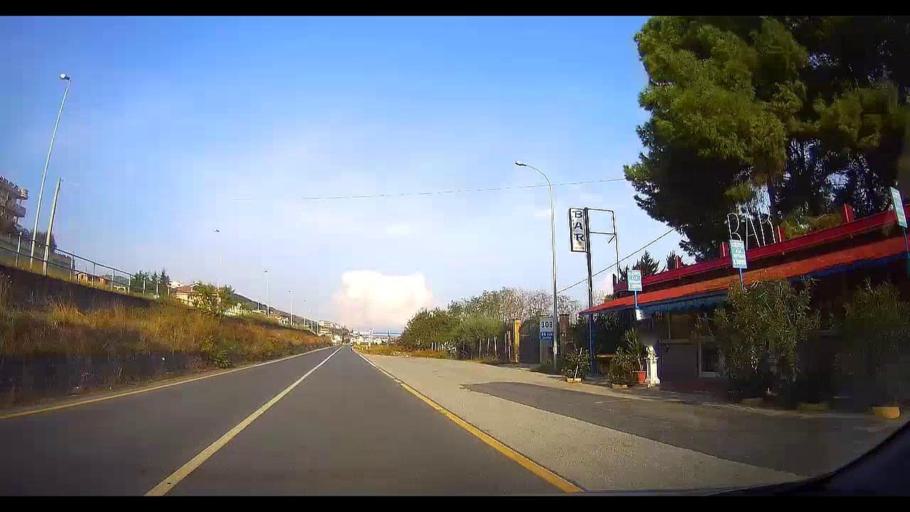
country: IT
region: Calabria
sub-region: Provincia di Cosenza
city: Cariati
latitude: 39.5245
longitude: 16.8935
